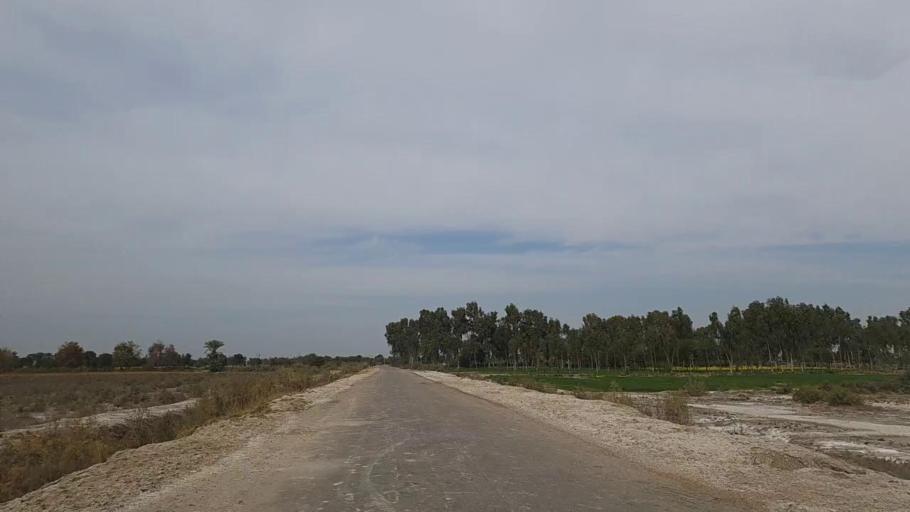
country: PK
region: Sindh
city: Daur
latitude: 26.4240
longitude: 68.4809
